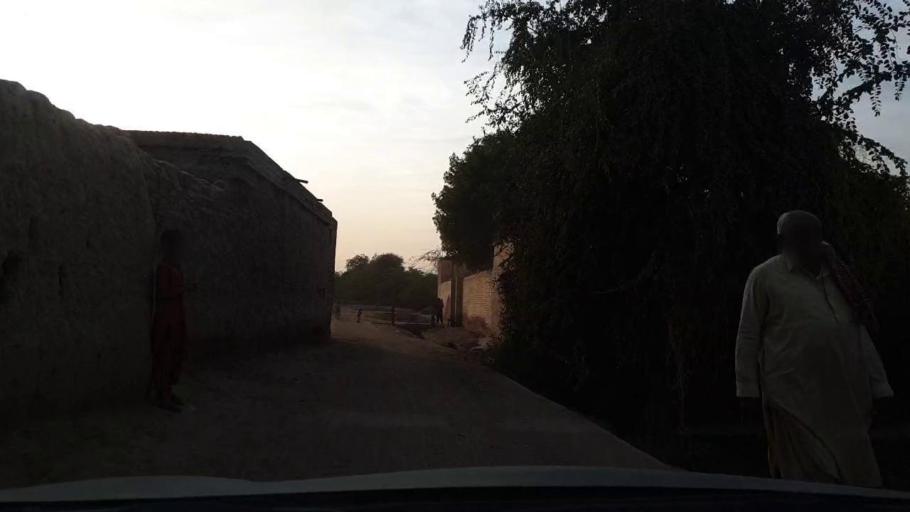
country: PK
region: Sindh
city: Tando Adam
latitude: 25.6857
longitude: 68.7143
